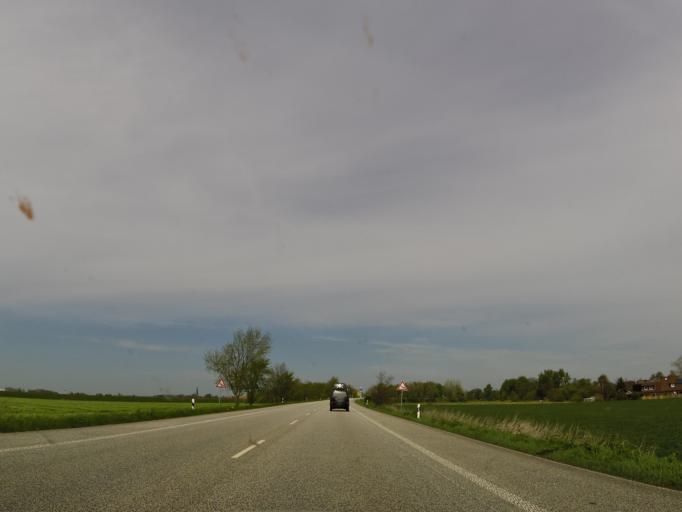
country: DE
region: Schleswig-Holstein
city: Karolinenkoog
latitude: 54.3042
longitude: 8.9622
